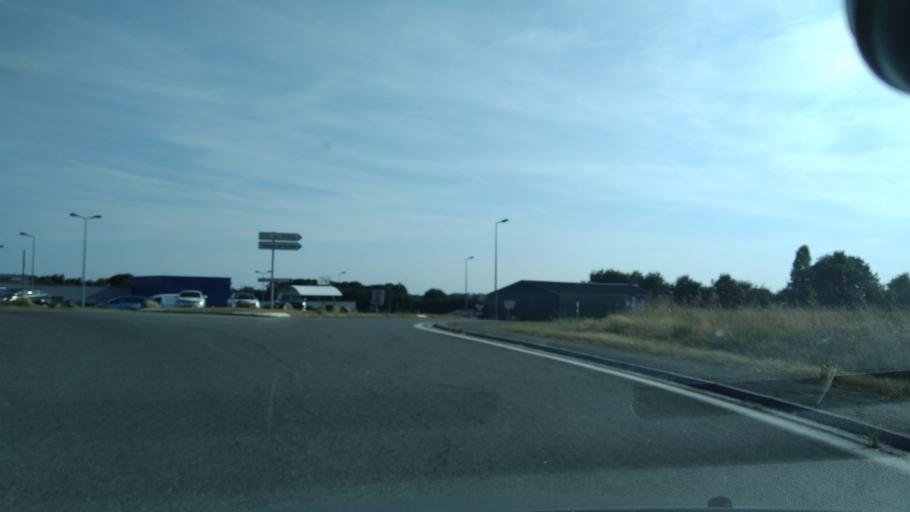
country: FR
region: Pays de la Loire
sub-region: Departement de la Mayenne
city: Entrammes
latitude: 48.0151
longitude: -0.7302
